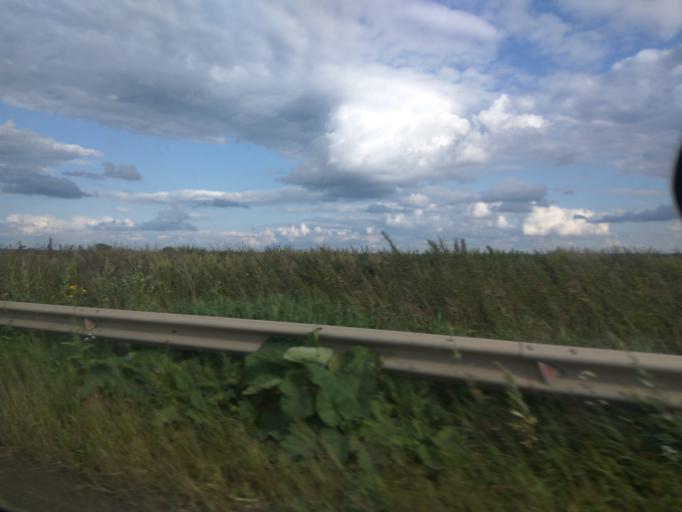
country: RU
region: Moskovskaya
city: Ramenskoye
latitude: 55.5009
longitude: 38.2409
